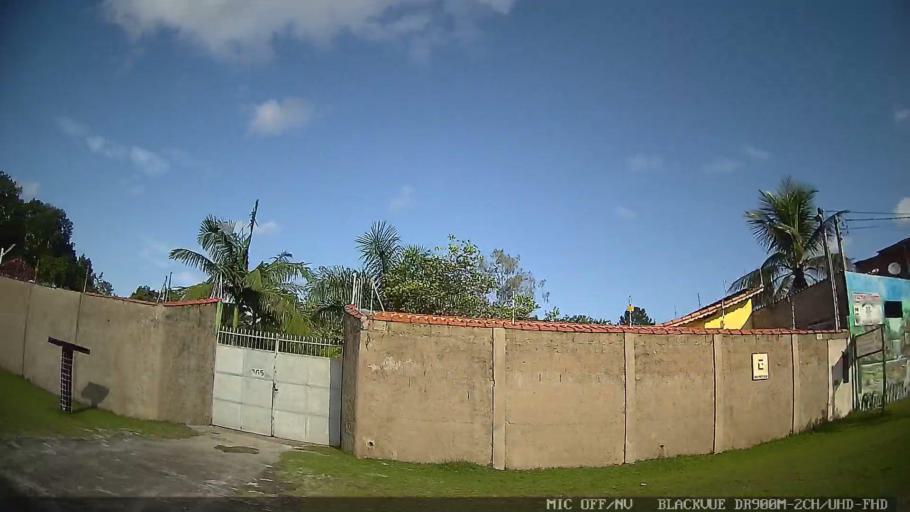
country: BR
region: Sao Paulo
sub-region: Itanhaem
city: Itanhaem
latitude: -24.1678
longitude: -46.8403
